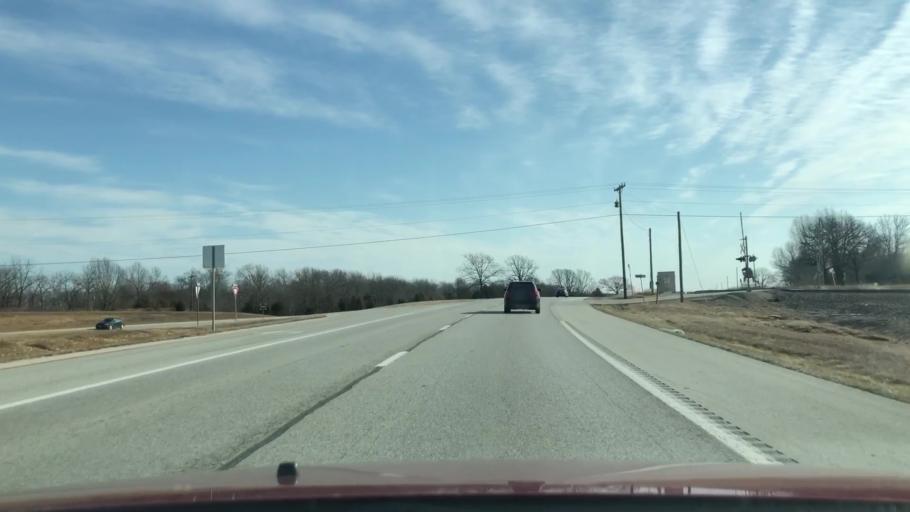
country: US
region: Missouri
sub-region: Webster County
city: Seymour
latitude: 37.1308
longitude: -92.7205
